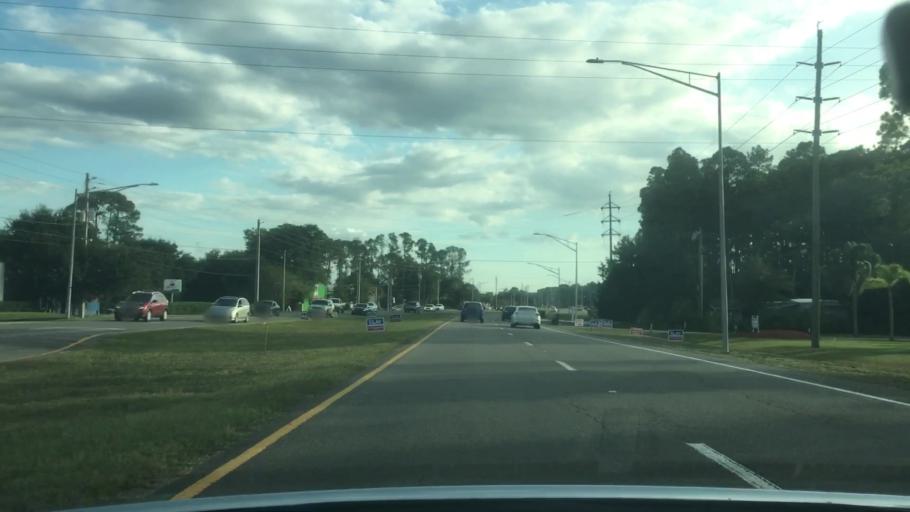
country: US
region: Florida
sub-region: Duval County
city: Atlantic Beach
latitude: 30.3123
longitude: -81.5254
